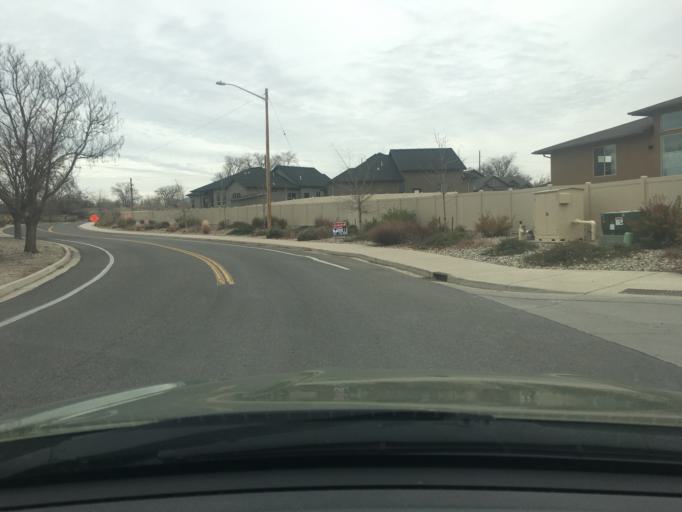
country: US
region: Colorado
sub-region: Mesa County
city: Grand Junction
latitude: 39.1128
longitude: -108.5728
